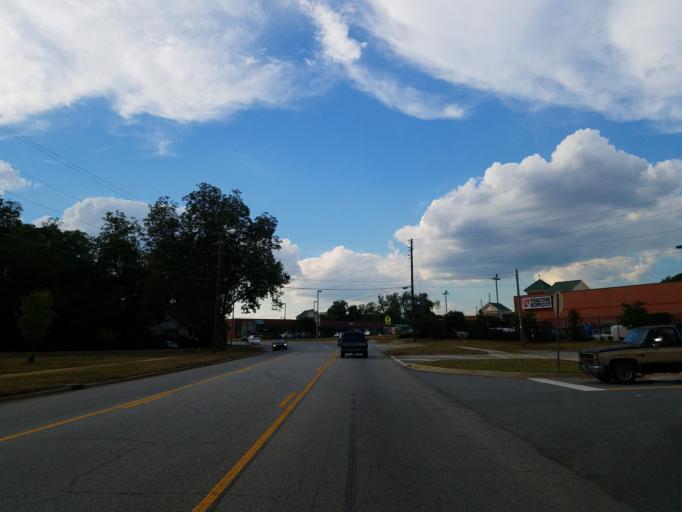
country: US
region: Georgia
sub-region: Monroe County
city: Forsyth
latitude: 33.0335
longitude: -83.9331
